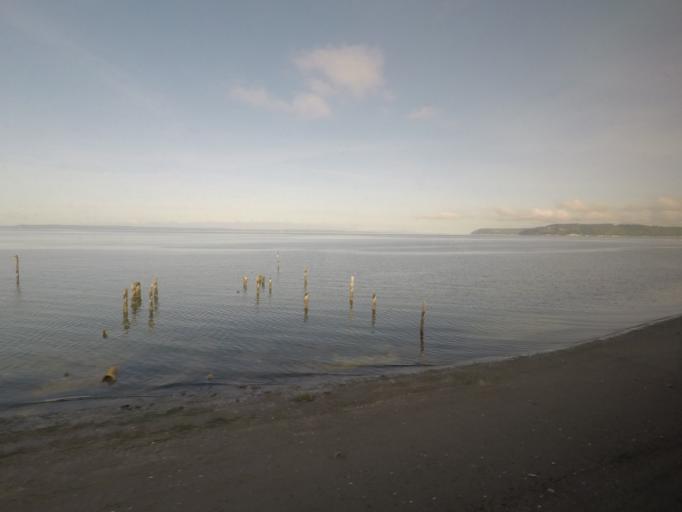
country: US
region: Washington
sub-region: Snohomish County
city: Meadowdale
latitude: 47.8757
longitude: -122.3298
